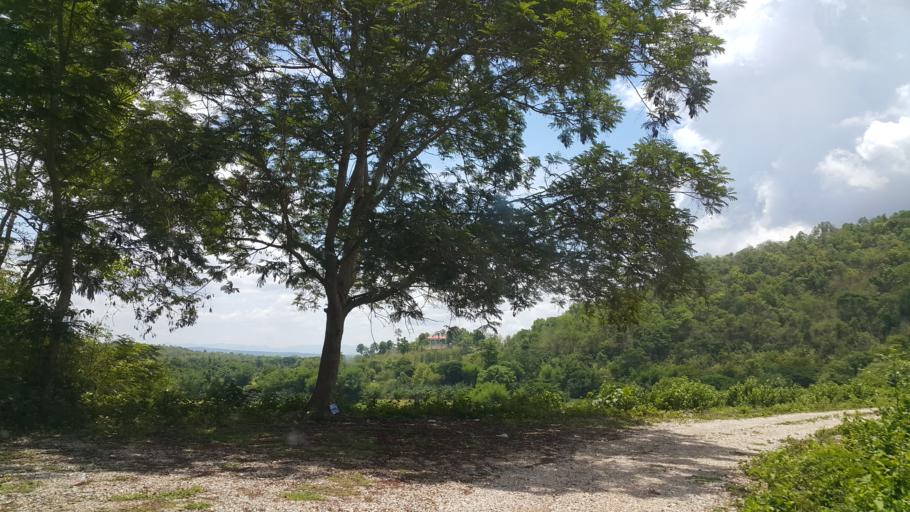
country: TH
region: Phayao
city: Phayao
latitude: 19.1859
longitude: 99.7996
